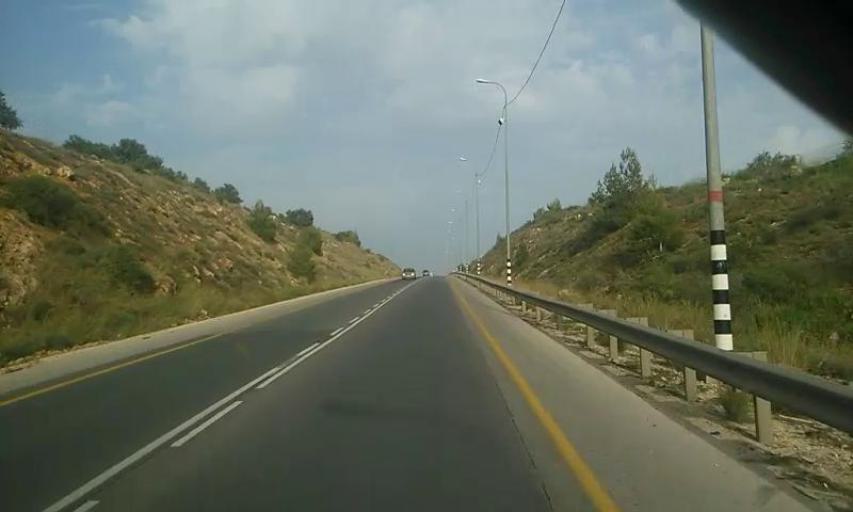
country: PS
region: West Bank
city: `Azzun
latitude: 32.1818
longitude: 35.0462
